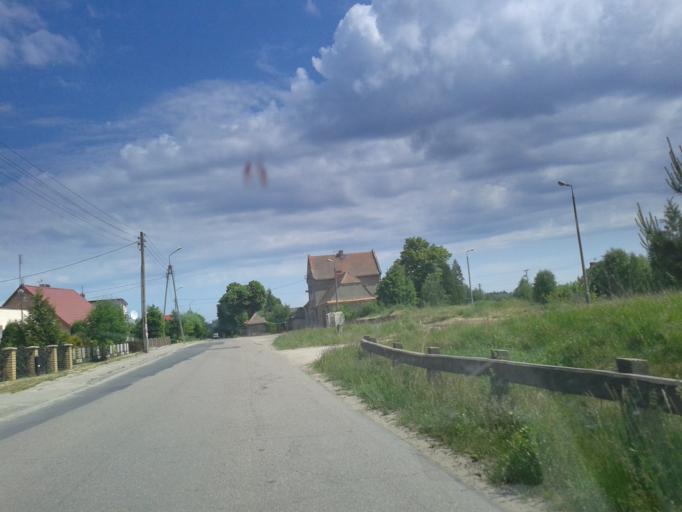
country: PL
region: Pomeranian Voivodeship
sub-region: Powiat koscierski
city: Karsin
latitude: 53.8961
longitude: 17.9291
